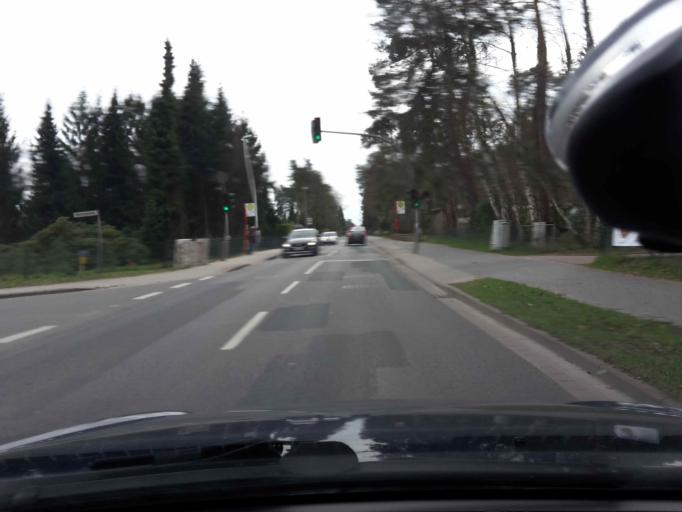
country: DE
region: Lower Saxony
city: Buchholz in der Nordheide
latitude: 53.2918
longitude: 9.8703
